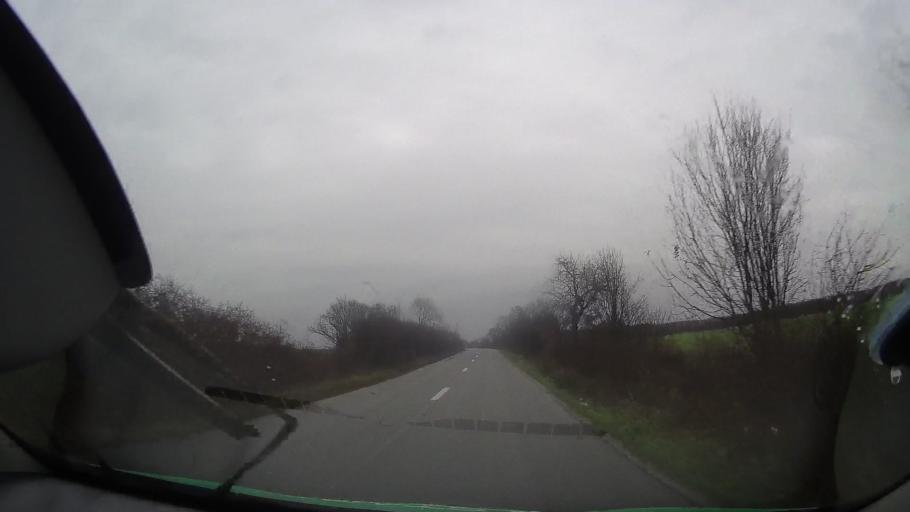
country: RO
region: Bihor
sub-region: Comuna Tinca
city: Tinca
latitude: 46.7419
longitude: 21.9572
